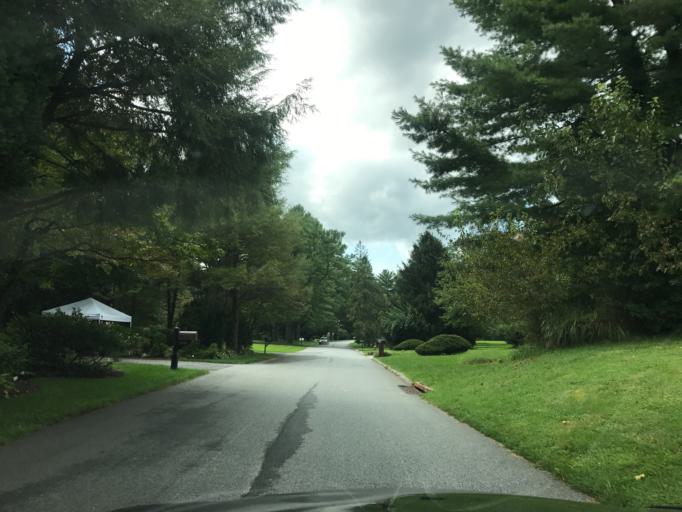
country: US
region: Maryland
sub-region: Baltimore County
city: Mays Chapel
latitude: 39.4133
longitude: -76.6518
